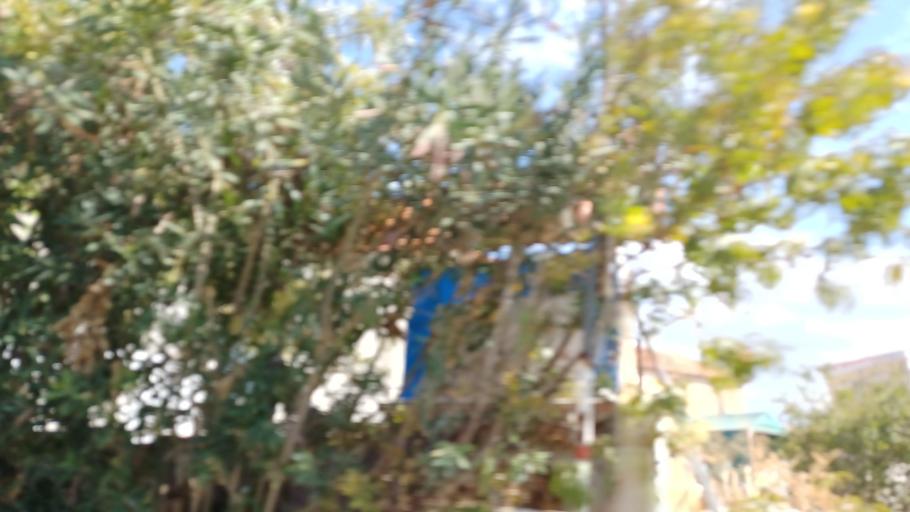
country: CY
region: Pafos
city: Polis
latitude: 35.0354
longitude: 32.4231
